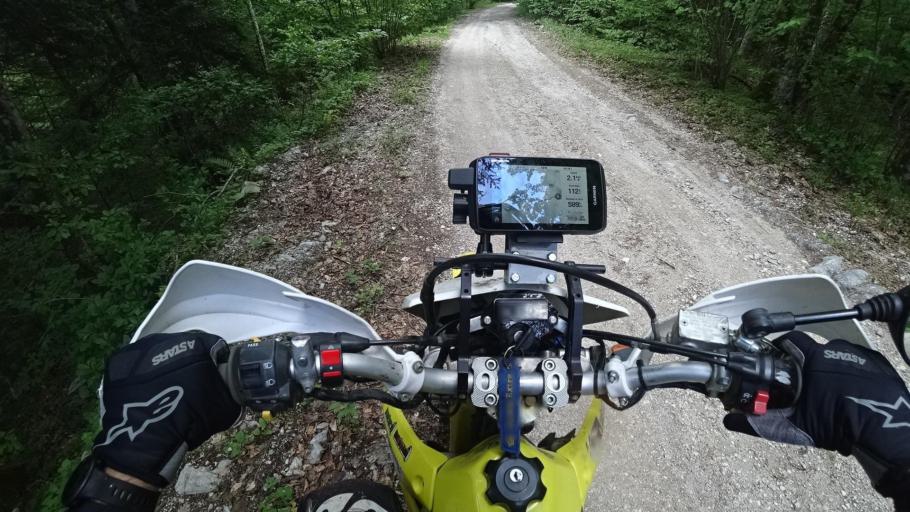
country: BA
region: Federation of Bosnia and Herzegovina
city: Bosanska Krupa
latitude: 44.8042
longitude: 16.0903
